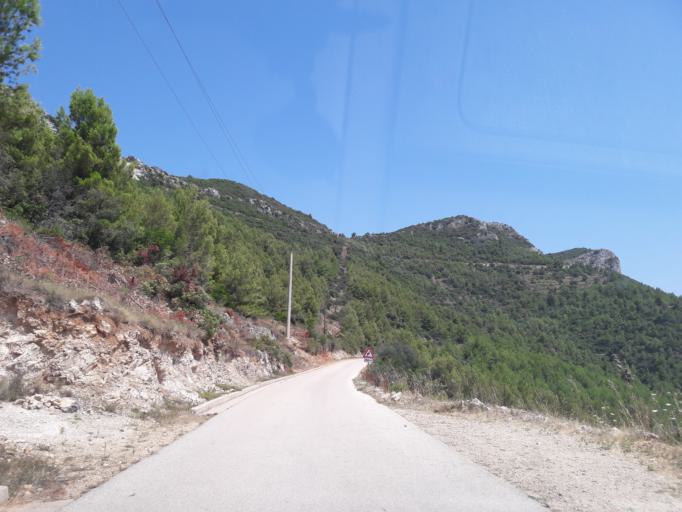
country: HR
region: Dubrovacko-Neretvanska
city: Blato
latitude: 42.9124
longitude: 17.4180
